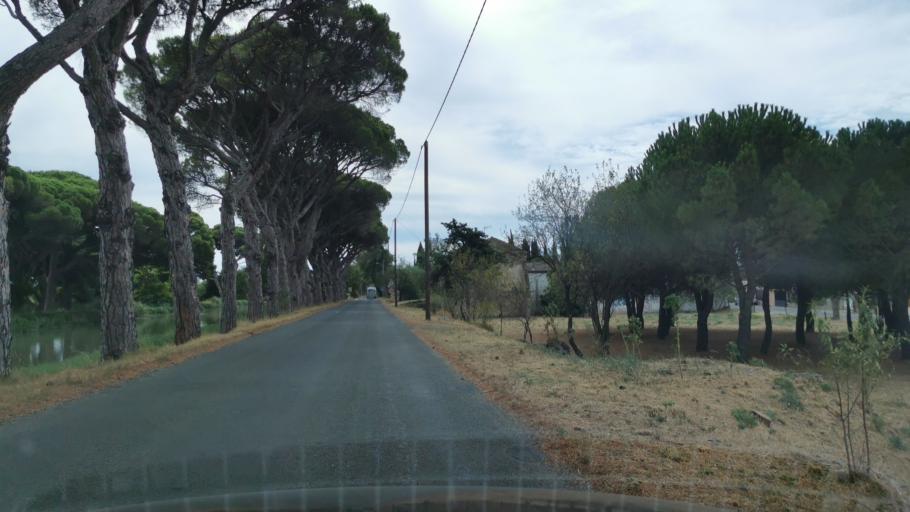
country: FR
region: Languedoc-Roussillon
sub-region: Departement de l'Aude
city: Saint-Marcel-sur-Aude
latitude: 43.2644
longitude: 2.9424
